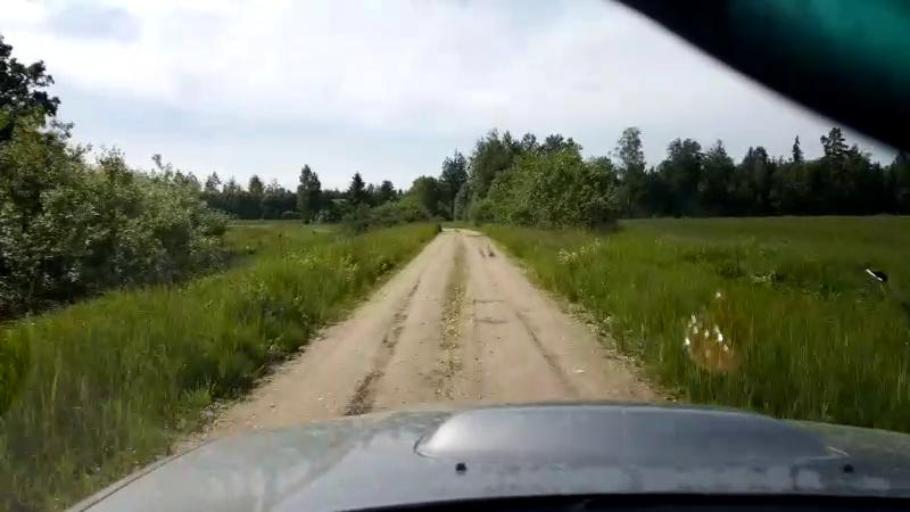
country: EE
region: Paernumaa
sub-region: Sindi linn
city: Sindi
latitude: 58.5275
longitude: 24.6693
